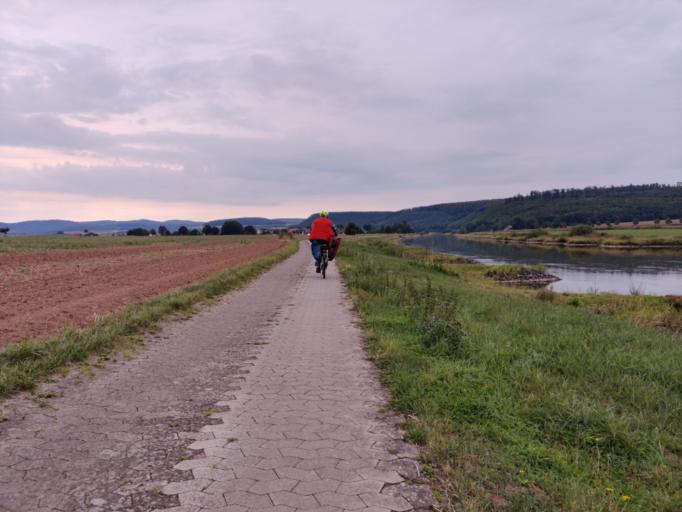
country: DE
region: Lower Saxony
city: Hehlen
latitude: 52.0093
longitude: 9.4272
